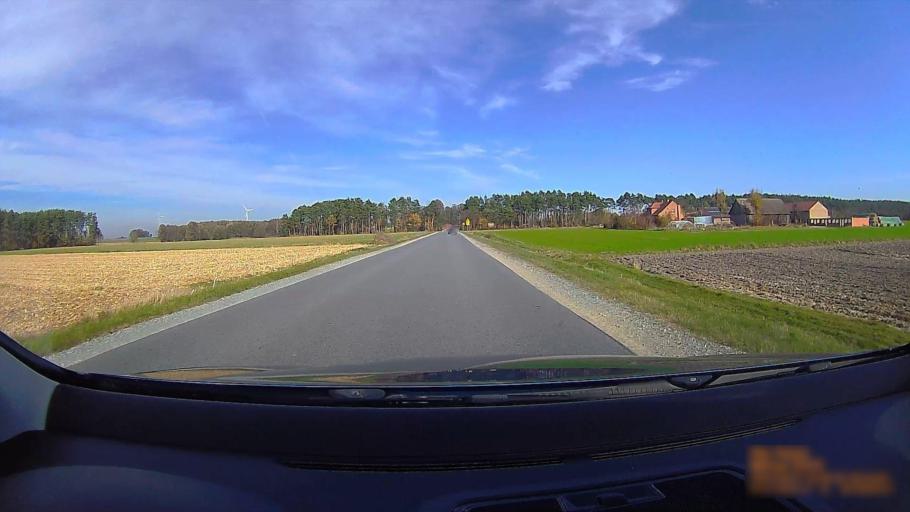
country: PL
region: Greater Poland Voivodeship
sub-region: Powiat ostrzeszowski
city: Doruchow
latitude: 51.3829
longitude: 18.0455
